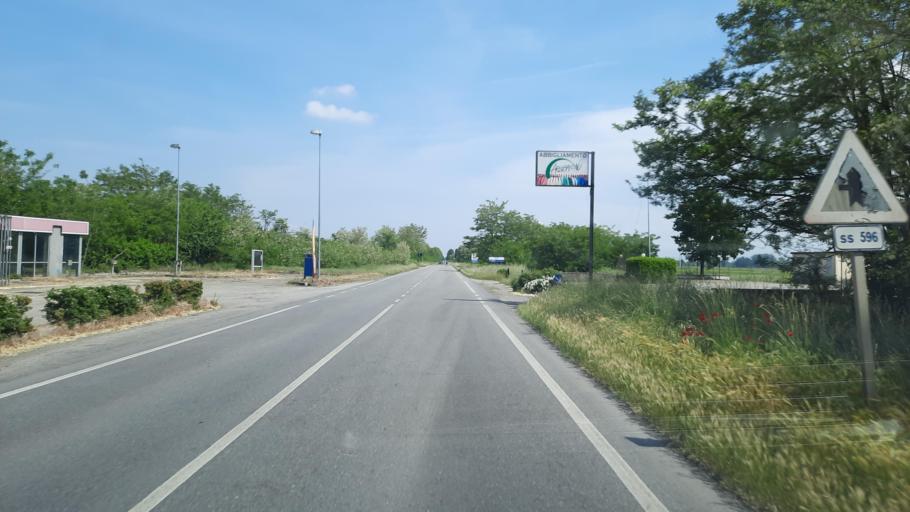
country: IT
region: Lombardy
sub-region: Provincia di Pavia
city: Garlasco
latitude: 45.1909
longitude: 8.9410
